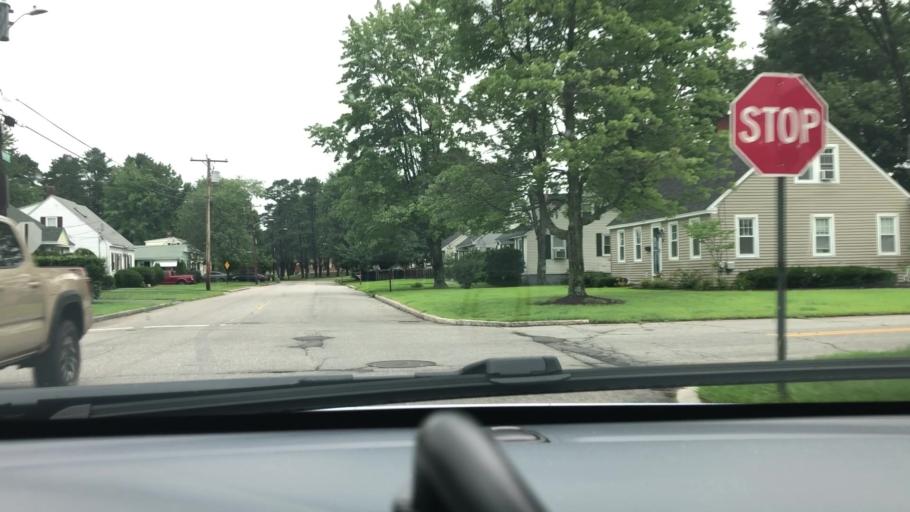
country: US
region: New Hampshire
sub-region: Hillsborough County
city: Pinardville
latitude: 42.9965
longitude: -71.4914
